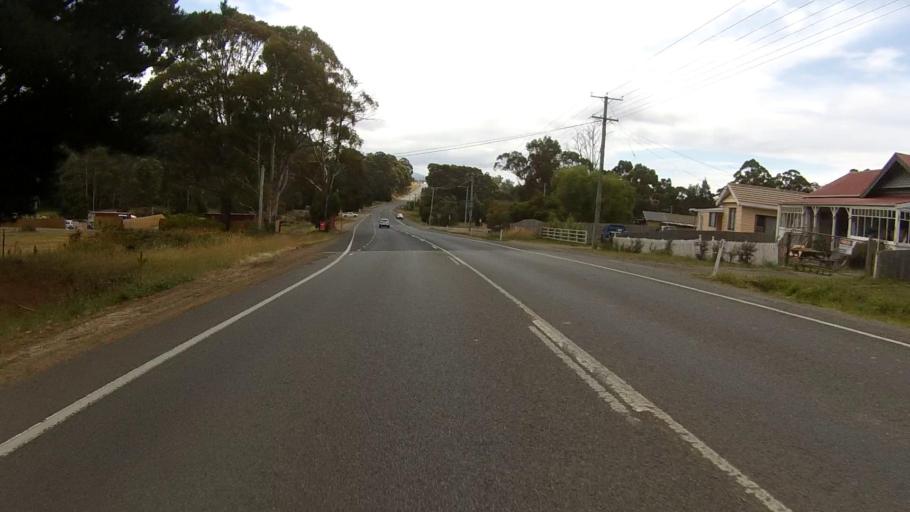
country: AU
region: Tasmania
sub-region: Kingborough
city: Margate
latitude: -43.0755
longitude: 147.2568
